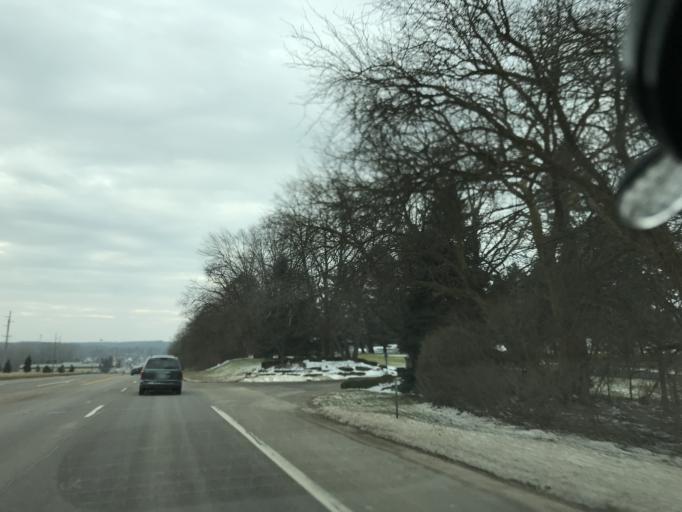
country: US
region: Michigan
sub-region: Kent County
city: Northview
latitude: 43.0686
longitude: -85.5800
